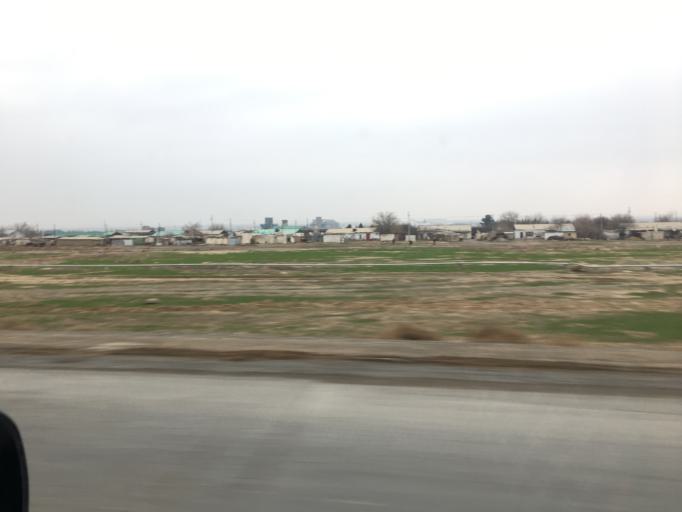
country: IR
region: Razavi Khorasan
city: Dargaz
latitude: 37.7658
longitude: 58.9027
